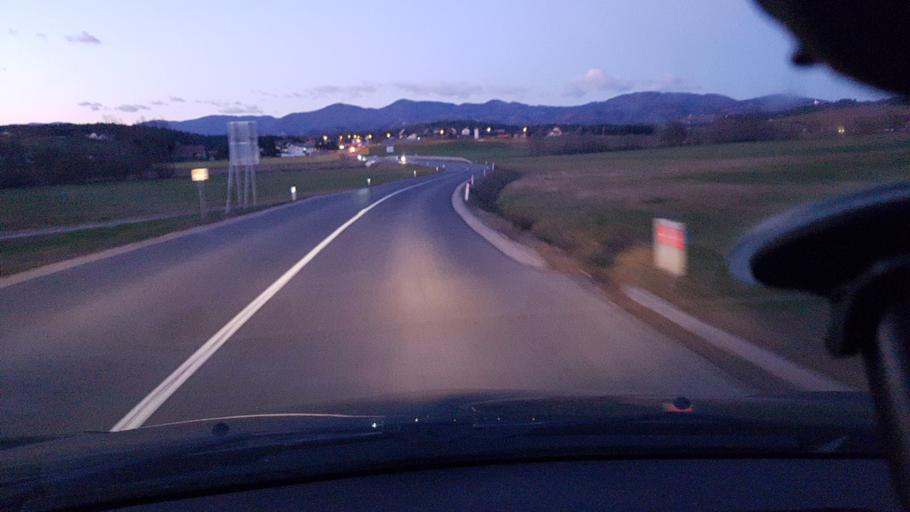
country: SI
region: Sentjur pri Celju
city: Sentjur
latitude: 46.2339
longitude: 15.3852
